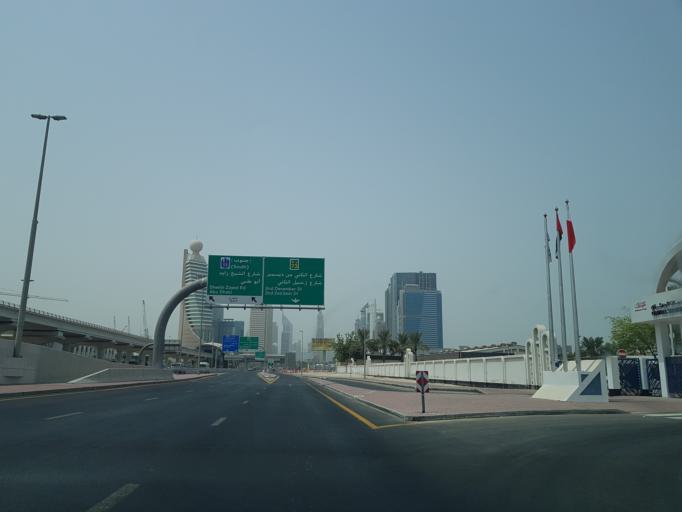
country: AE
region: Ash Shariqah
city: Sharjah
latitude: 25.2373
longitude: 55.2937
